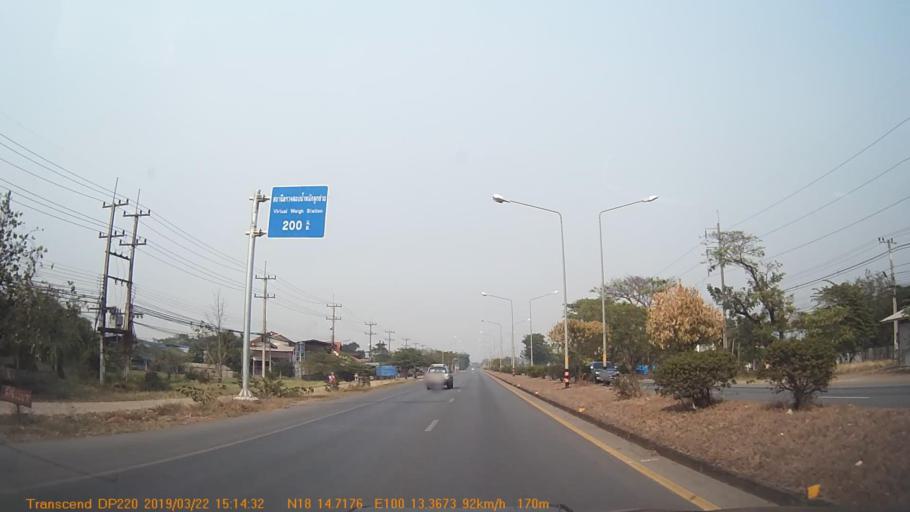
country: TH
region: Phrae
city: Nong Muang Khai
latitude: 18.2457
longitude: 100.2231
